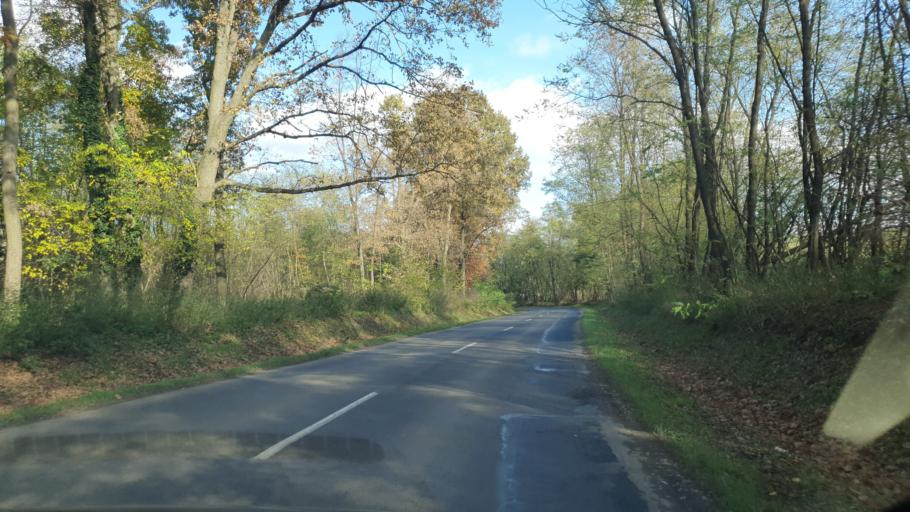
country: HU
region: Szabolcs-Szatmar-Bereg
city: Anarcs
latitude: 48.1600
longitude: 22.0956
